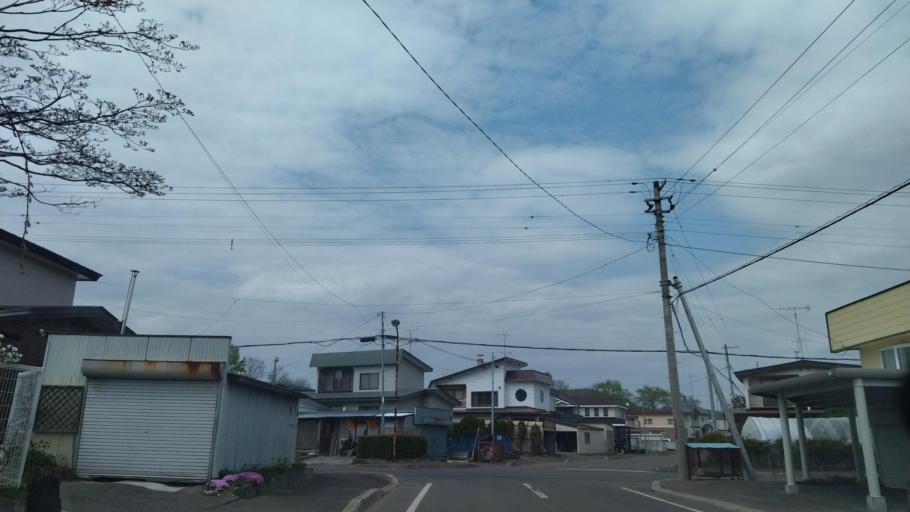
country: JP
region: Hokkaido
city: Otofuke
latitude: 43.2362
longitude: 143.5573
